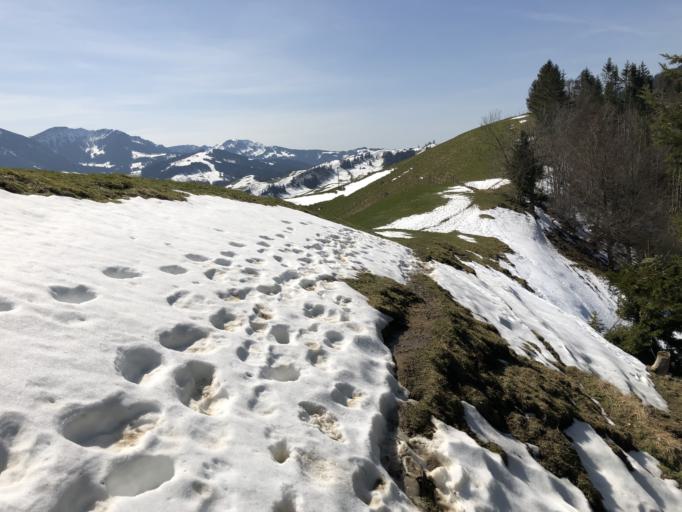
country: CH
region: Appenzell Innerrhoden
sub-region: Appenzell Inner Rhodes
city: Gonten
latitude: 47.3415
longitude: 9.3614
